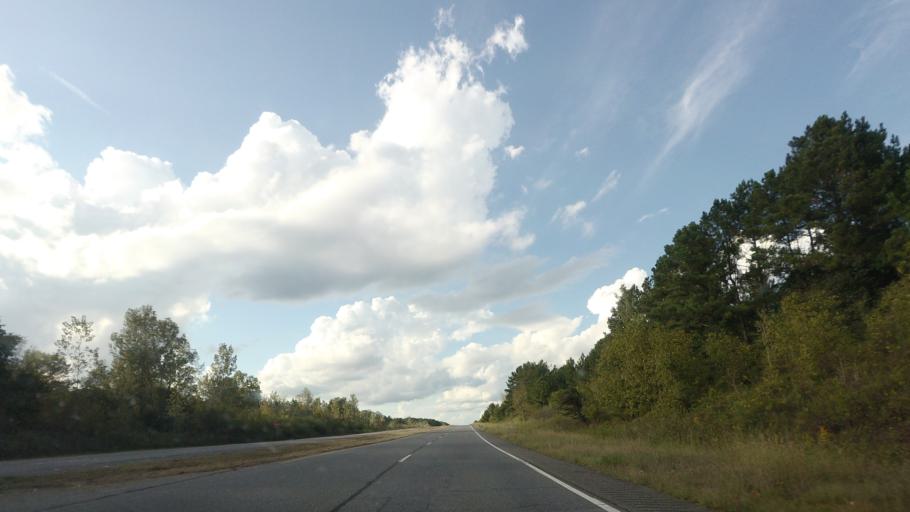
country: US
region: Georgia
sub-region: Houston County
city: Perry
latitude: 32.3998
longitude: -83.6425
